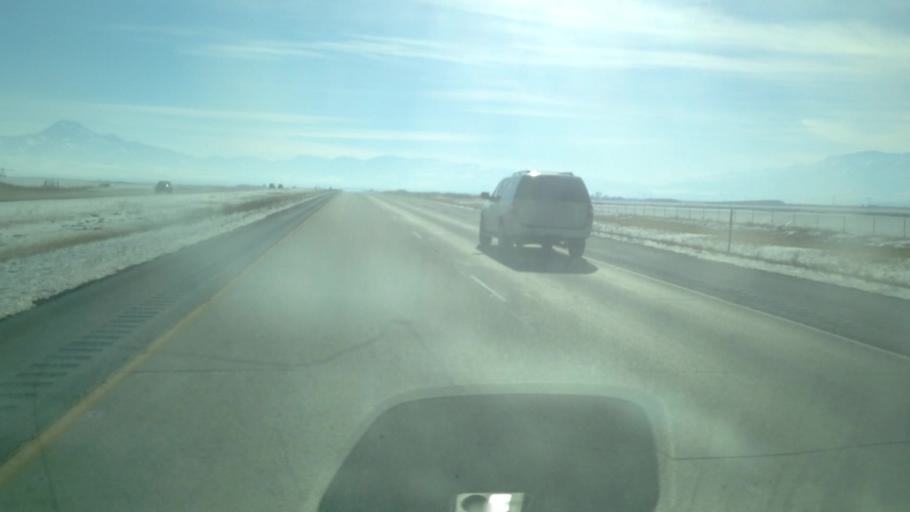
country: US
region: Idaho
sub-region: Oneida County
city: Malad City
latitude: 42.4728
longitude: -112.1697
